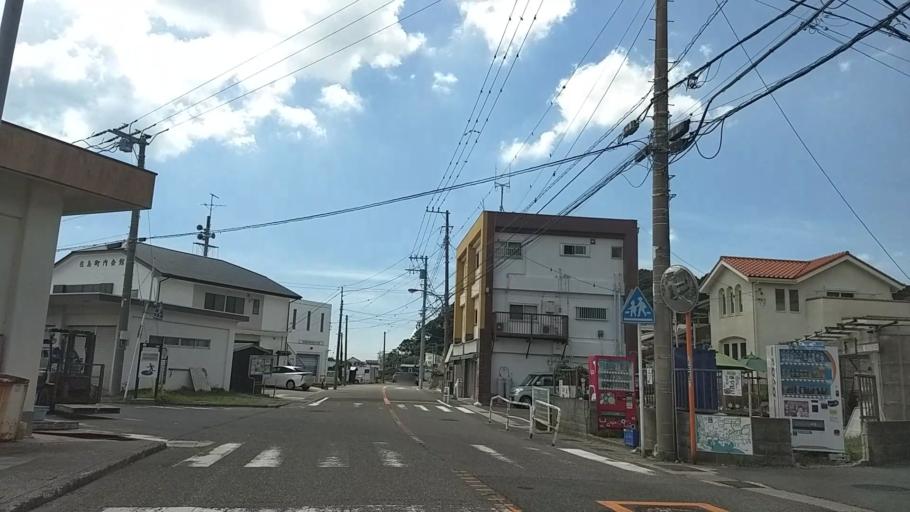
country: JP
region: Kanagawa
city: Hayama
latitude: 35.2236
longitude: 139.6093
